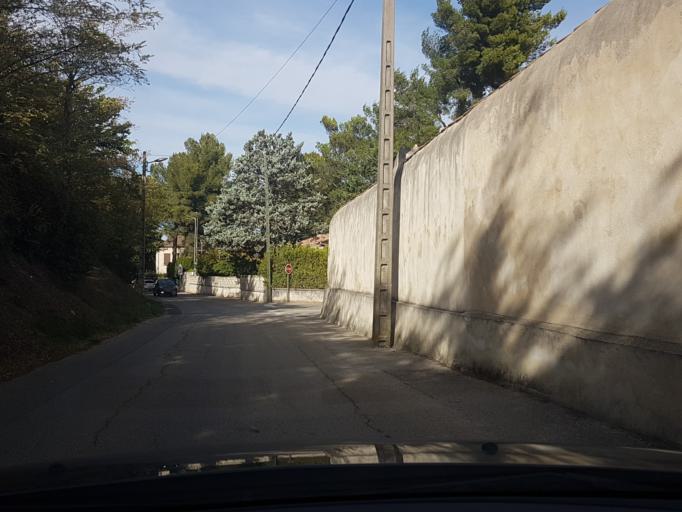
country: FR
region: Provence-Alpes-Cote d'Azur
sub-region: Departement du Vaucluse
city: Saint-Saturnin-les-Avignon
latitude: 43.9537
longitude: 4.9318
